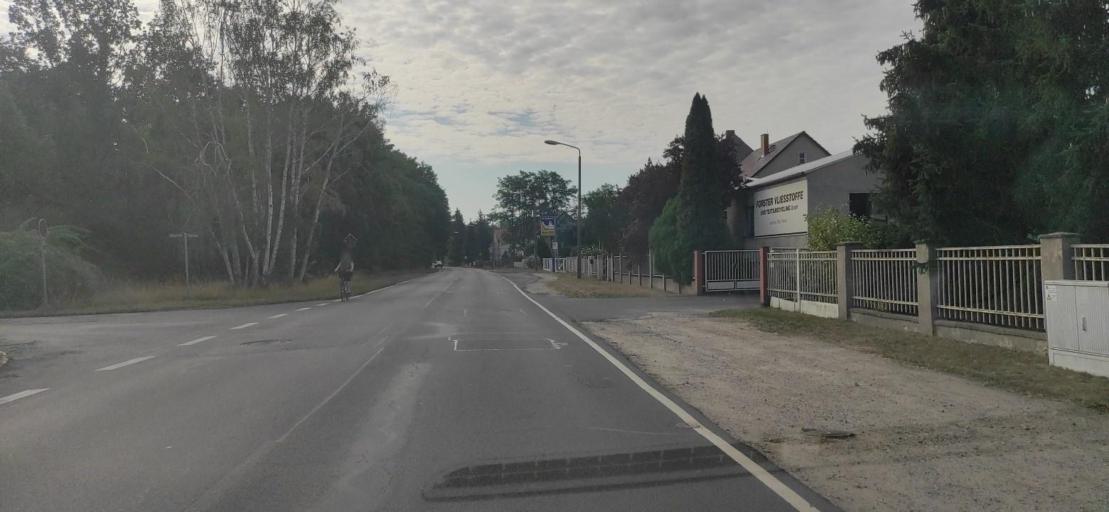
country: DE
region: Brandenburg
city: Forst
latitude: 51.7268
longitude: 14.6477
